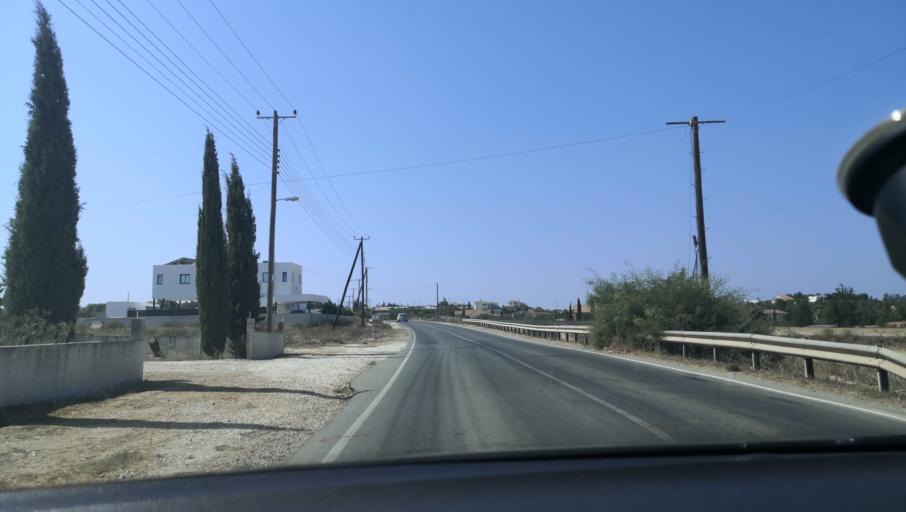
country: CY
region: Lefkosia
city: Kato Deftera
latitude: 35.1217
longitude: 33.2485
